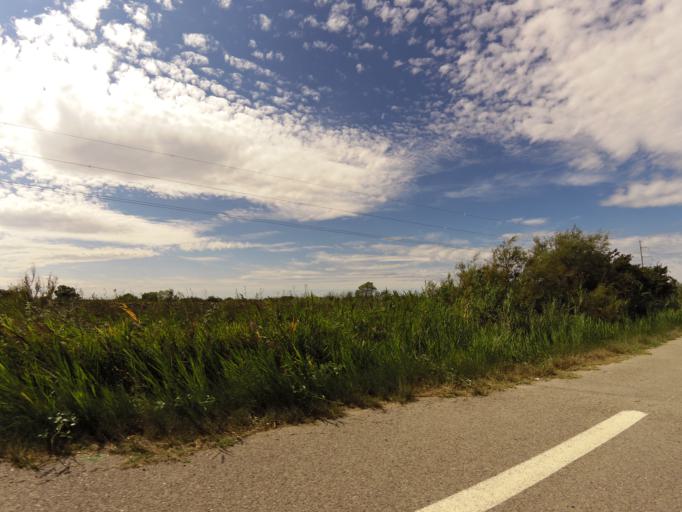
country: FR
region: Languedoc-Roussillon
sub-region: Departement du Gard
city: Aigues-Mortes
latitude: 43.6060
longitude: 4.1937
